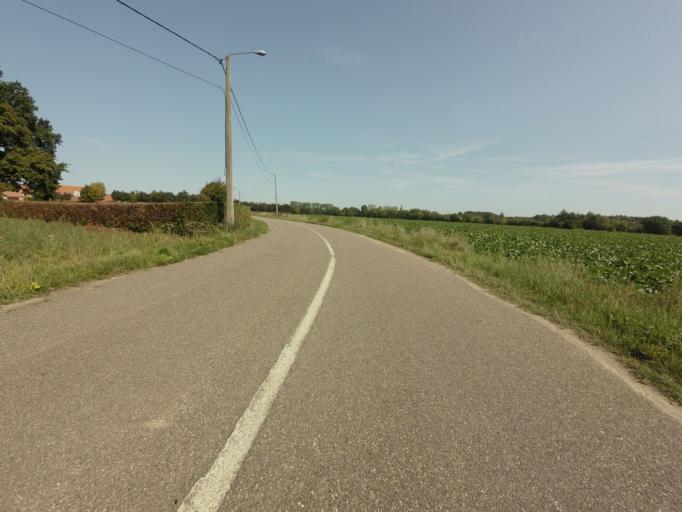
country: NL
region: Limburg
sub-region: Gemeente Maasgouw
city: Maasbracht
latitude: 51.1534
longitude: 5.8289
